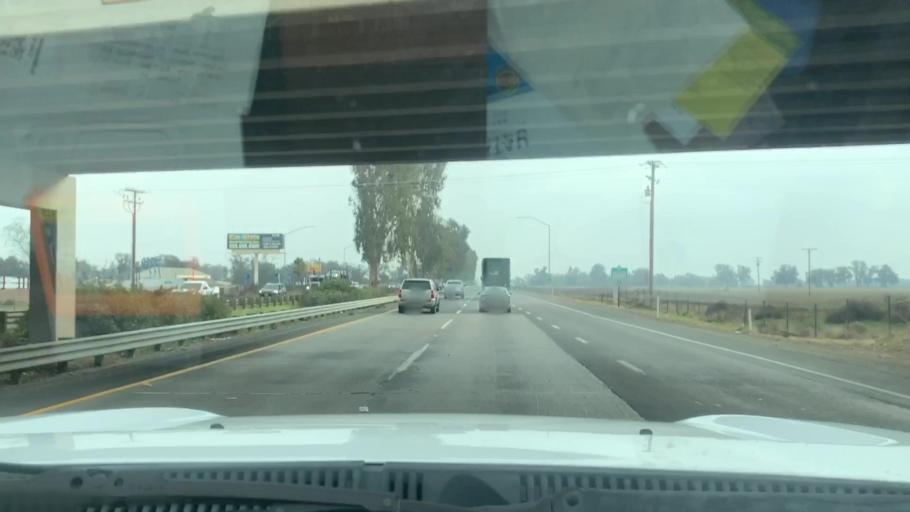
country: US
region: California
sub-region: Tulare County
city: Tulare
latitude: 36.1511
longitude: -119.3312
